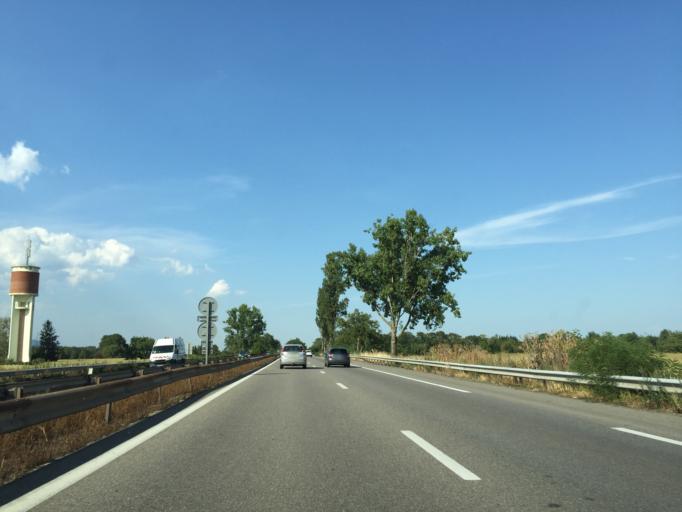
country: FR
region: Alsace
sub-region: Departement du Haut-Rhin
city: Guemar
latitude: 48.1819
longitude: 7.3855
